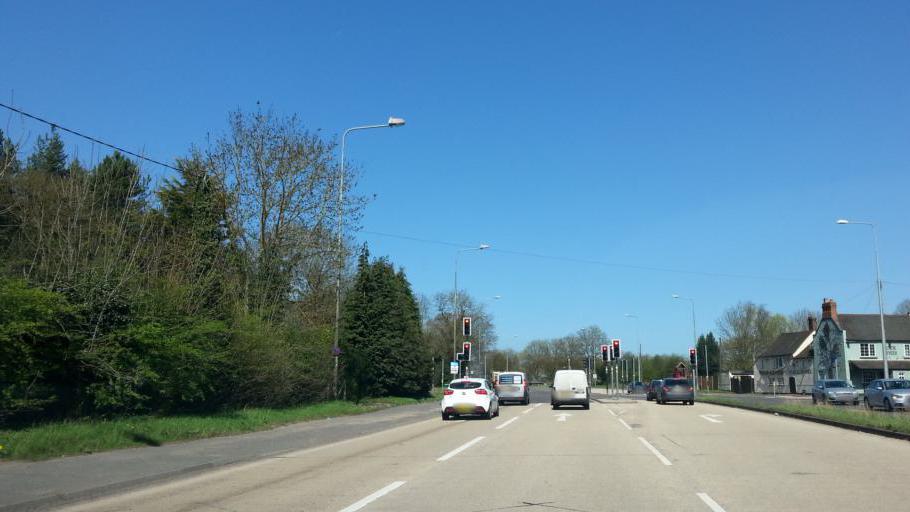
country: GB
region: England
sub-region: Staffordshire
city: Brewood
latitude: 52.6718
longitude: -2.1310
